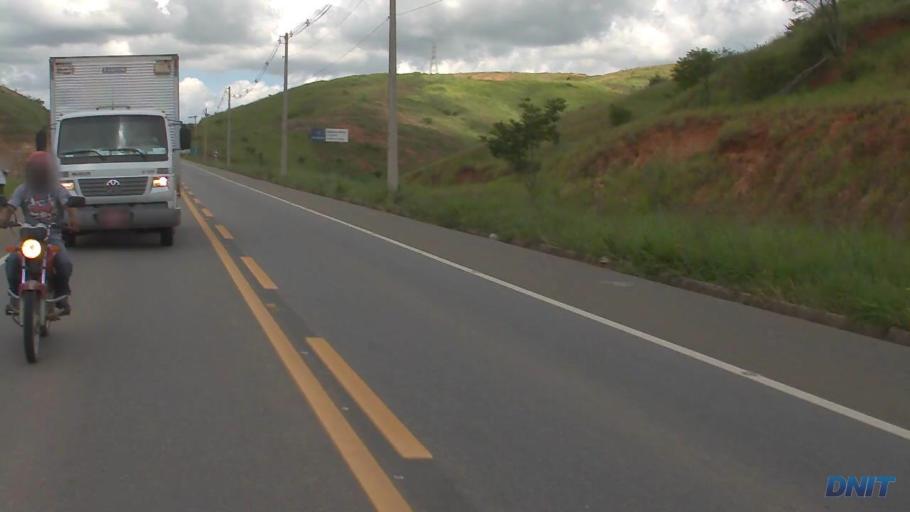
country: BR
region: Minas Gerais
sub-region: Governador Valadares
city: Governador Valadares
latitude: -18.8740
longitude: -41.9926
